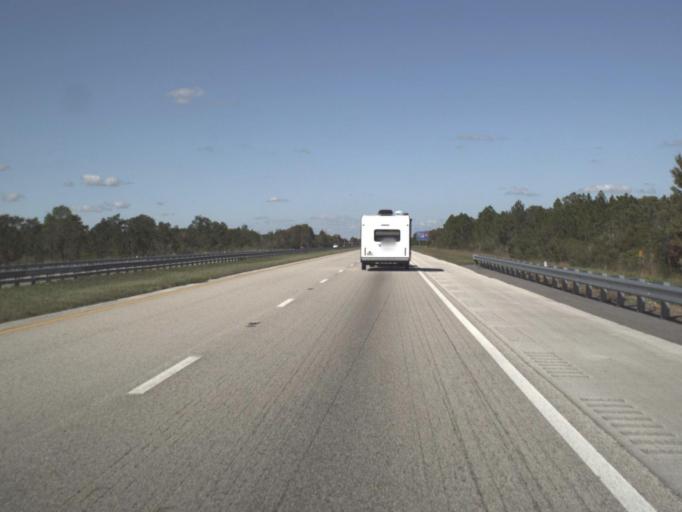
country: US
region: Florida
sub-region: Osceola County
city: Saint Cloud
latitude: 28.0041
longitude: -81.1452
